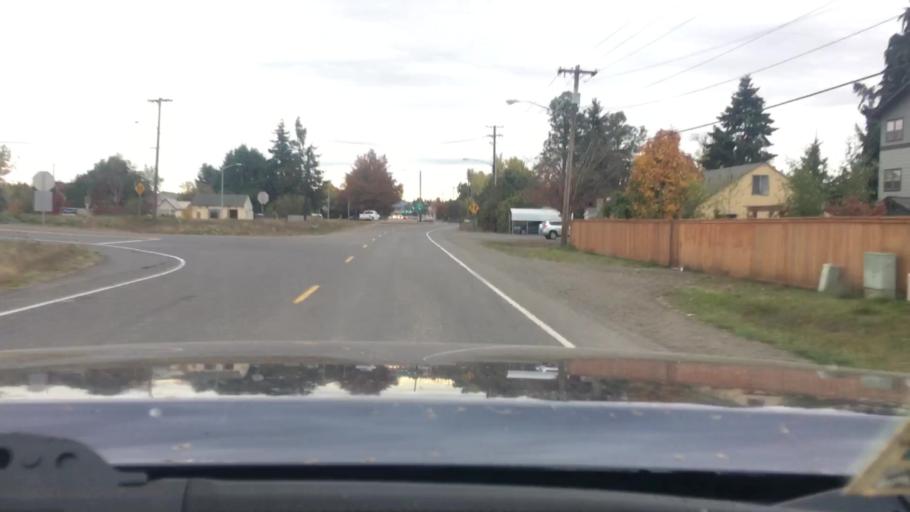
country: US
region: Oregon
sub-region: Lane County
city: Coburg
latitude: 44.0971
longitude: -123.0679
